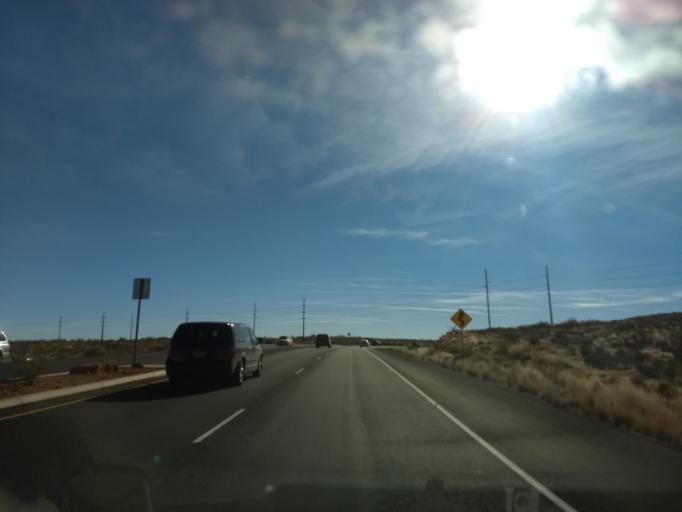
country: US
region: Utah
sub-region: Washington County
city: Saint George
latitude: 37.1273
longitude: -113.5829
